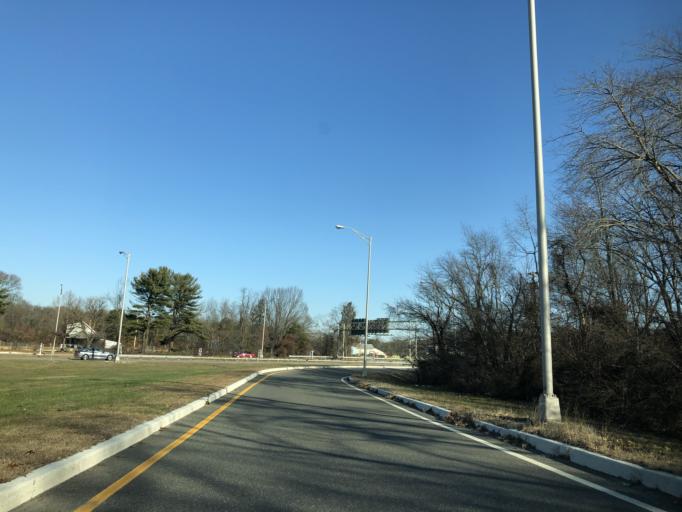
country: US
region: Pennsylvania
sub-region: Delaware County
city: Chester
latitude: 39.8022
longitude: -75.3464
